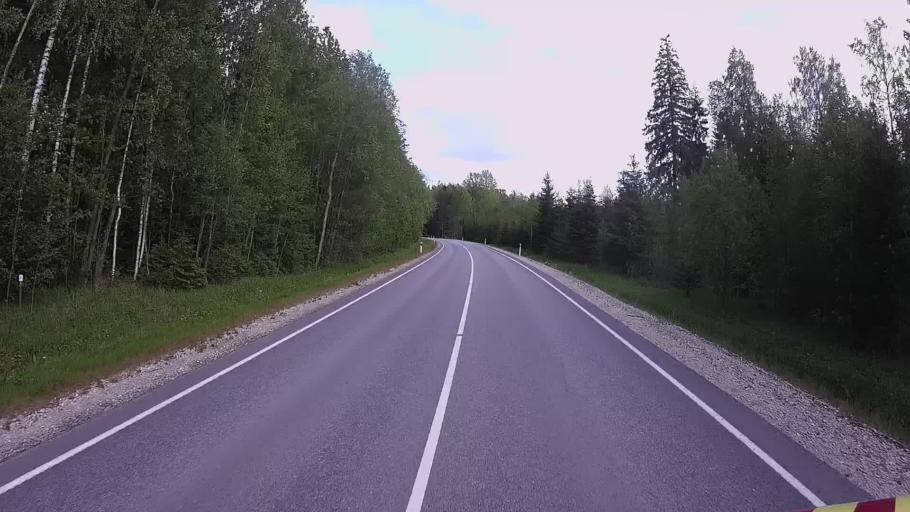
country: EE
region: Jogevamaa
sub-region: Mustvee linn
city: Mustvee
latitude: 58.8719
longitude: 26.8234
